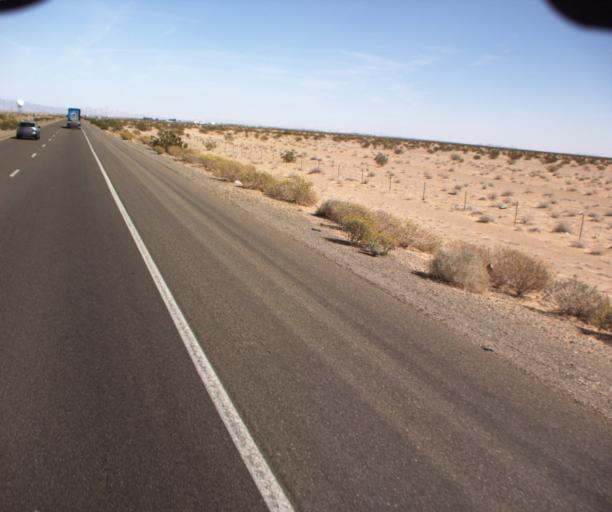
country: MX
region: Sonora
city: San Luis Rio Colorado
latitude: 32.4945
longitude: -114.6697
